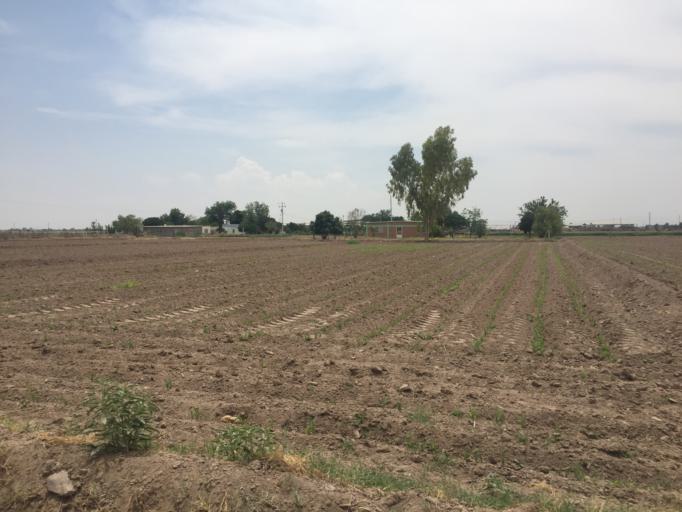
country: MX
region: Durango
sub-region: Gomez Palacio
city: San Jose de Vinedo
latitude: 25.6823
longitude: -103.4369
